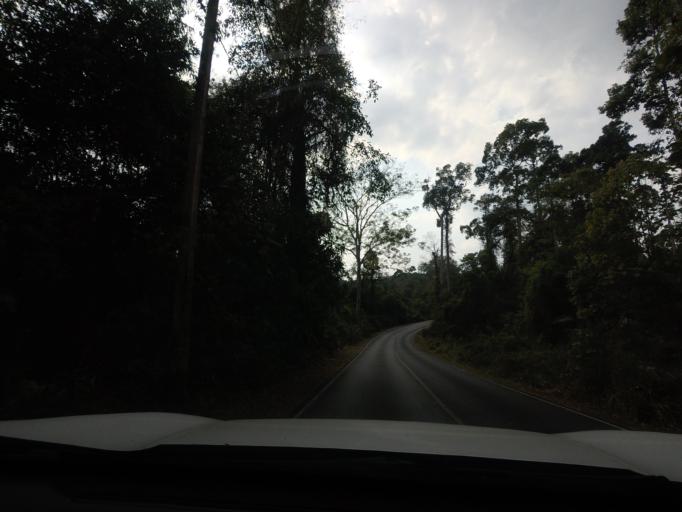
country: TH
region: Nakhon Ratchasima
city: Pak Chong
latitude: 14.4755
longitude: 101.3854
